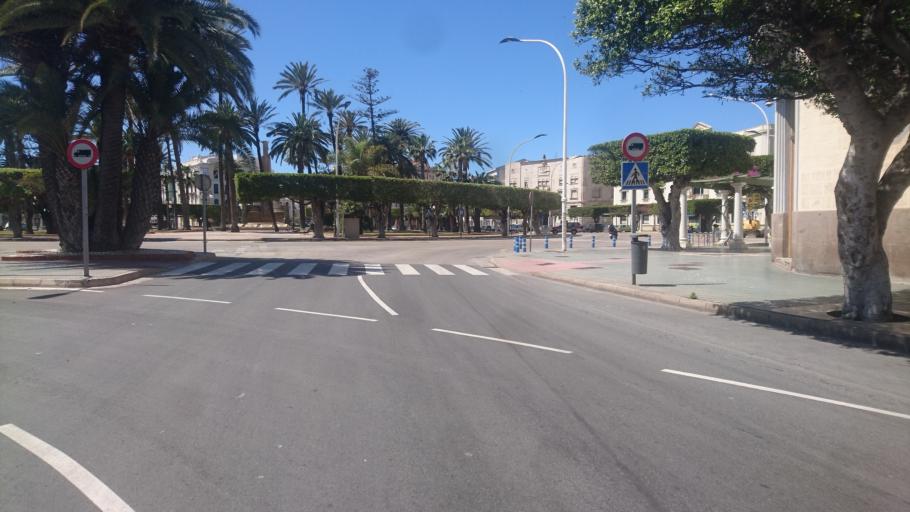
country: ES
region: Melilla
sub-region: Melilla
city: Melilla
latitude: 35.2917
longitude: -2.9370
